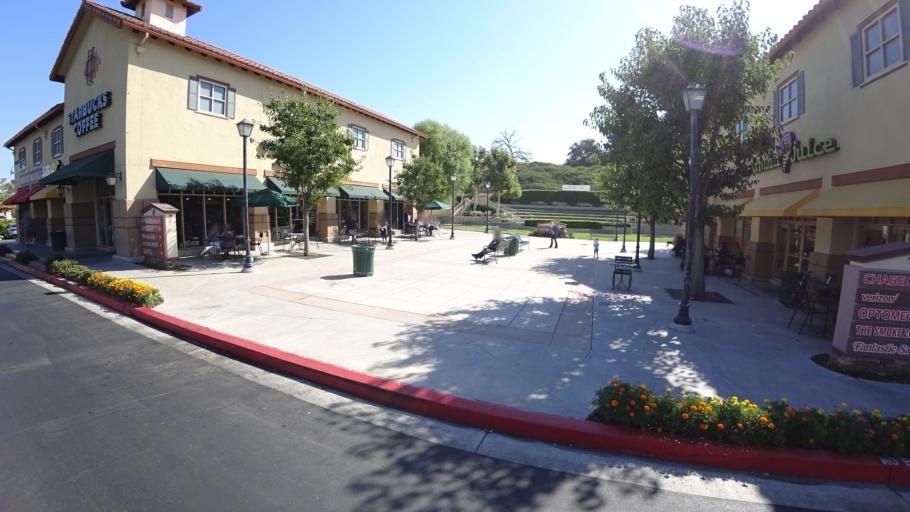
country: US
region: California
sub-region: Los Angeles County
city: Santa Clarita
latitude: 34.3920
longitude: -118.5733
